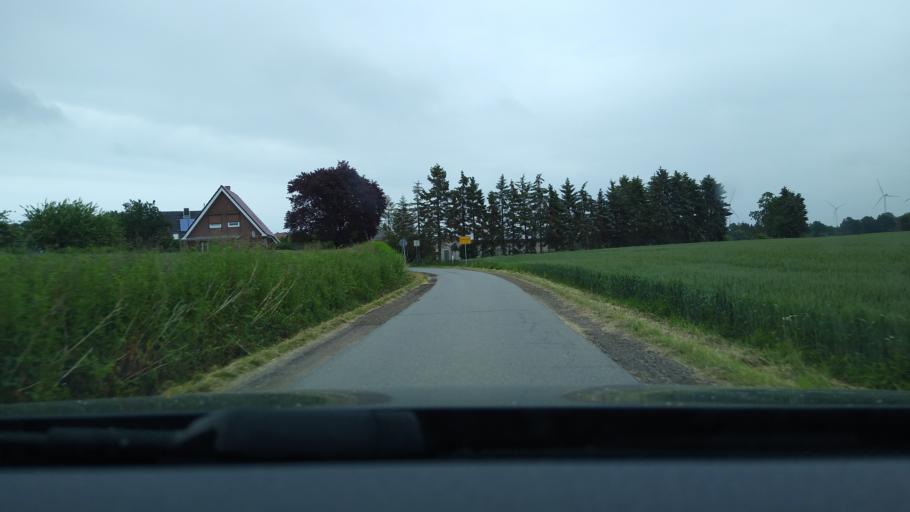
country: DE
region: Schleswig-Holstein
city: Kabelhorst
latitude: 54.2277
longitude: 10.9233
